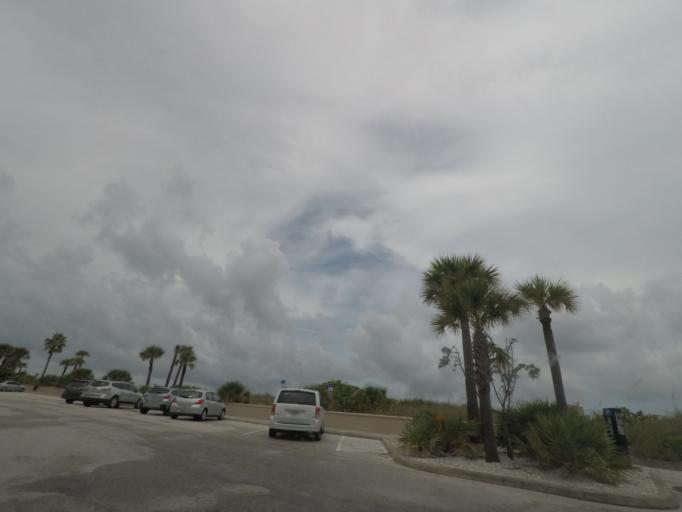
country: US
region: Florida
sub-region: Pinellas County
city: Tierra Verde
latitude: 27.6980
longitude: -82.7373
